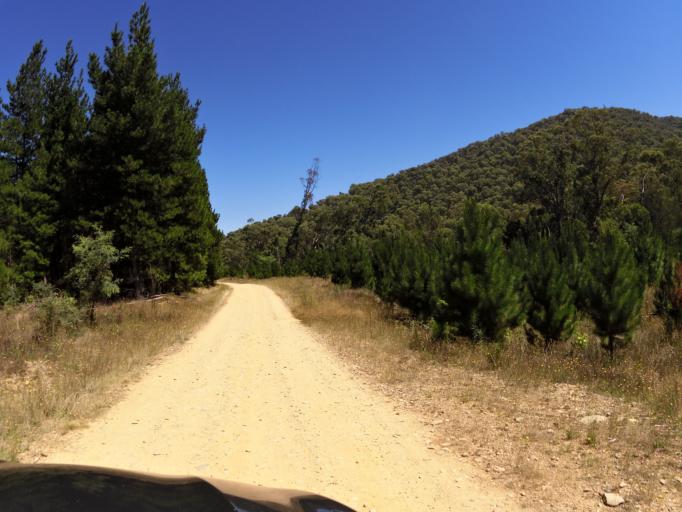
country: AU
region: Victoria
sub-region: Alpine
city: Mount Beauty
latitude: -36.7265
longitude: 146.9770
